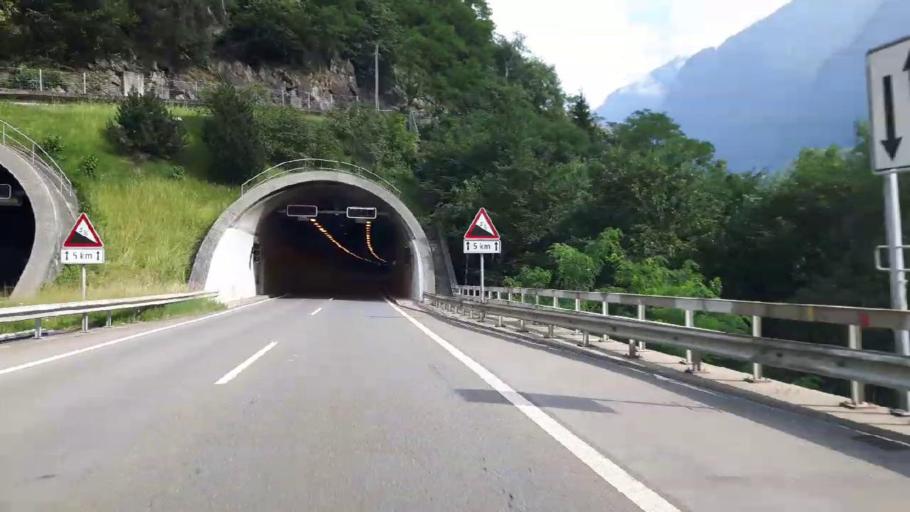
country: CH
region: Ticino
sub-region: Blenio District
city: Cancori
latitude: 46.4279
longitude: 8.8543
